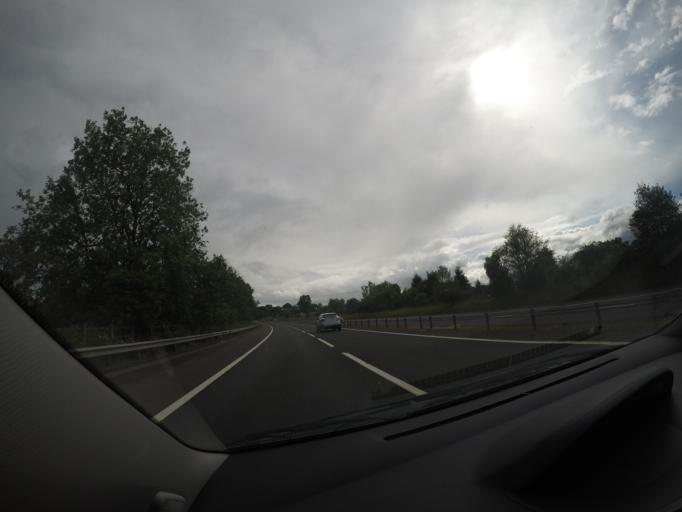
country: GB
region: Scotland
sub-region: Falkirk
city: Dunipace
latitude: 56.0335
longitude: -3.9229
